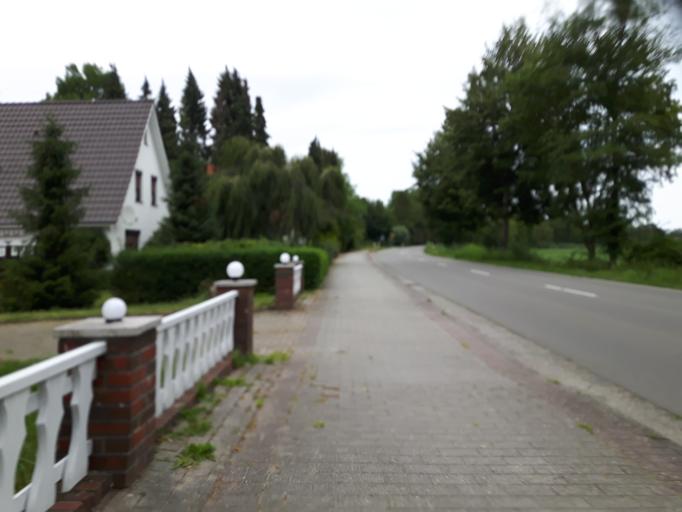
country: DE
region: Lower Saxony
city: Varel
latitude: 53.3870
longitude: 8.2416
